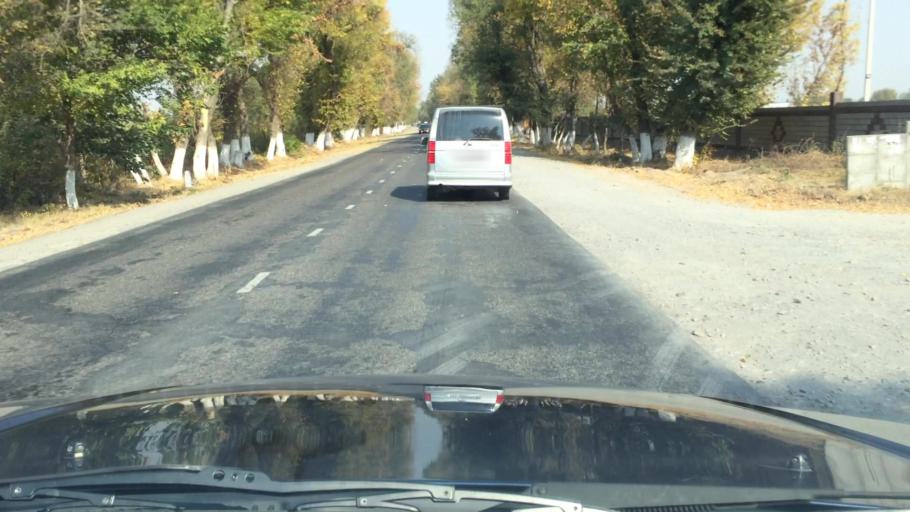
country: KG
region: Chuy
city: Lebedinovka
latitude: 42.9240
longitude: 74.6902
